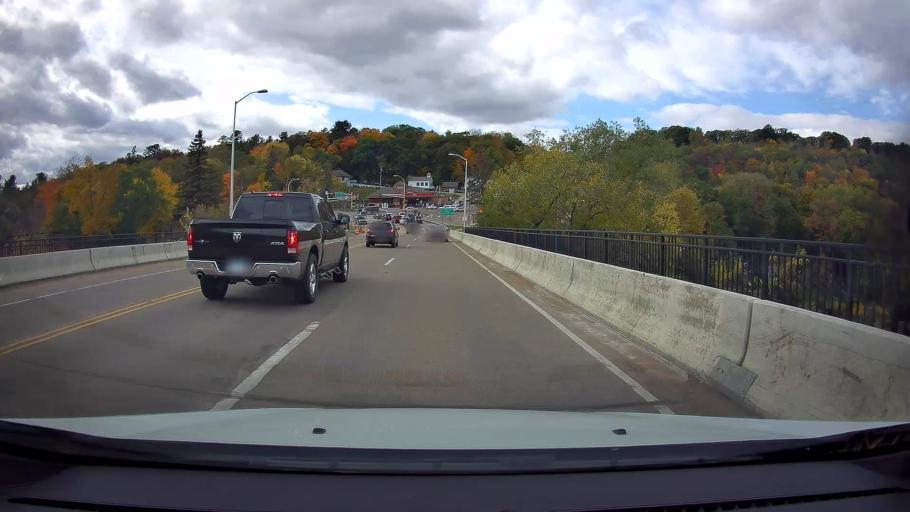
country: US
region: Wisconsin
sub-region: Polk County
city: Saint Croix Falls
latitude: 45.4020
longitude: -92.6502
